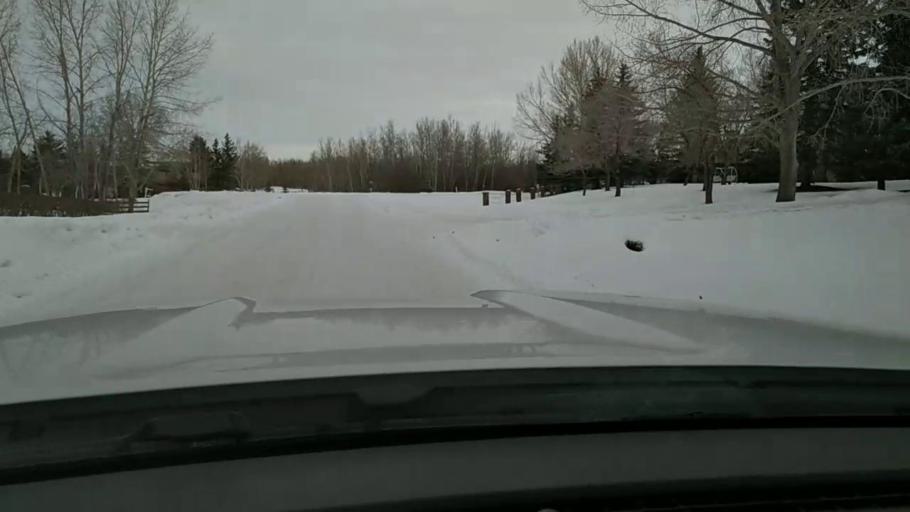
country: CA
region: Alberta
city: Calgary
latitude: 51.1182
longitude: -114.2668
